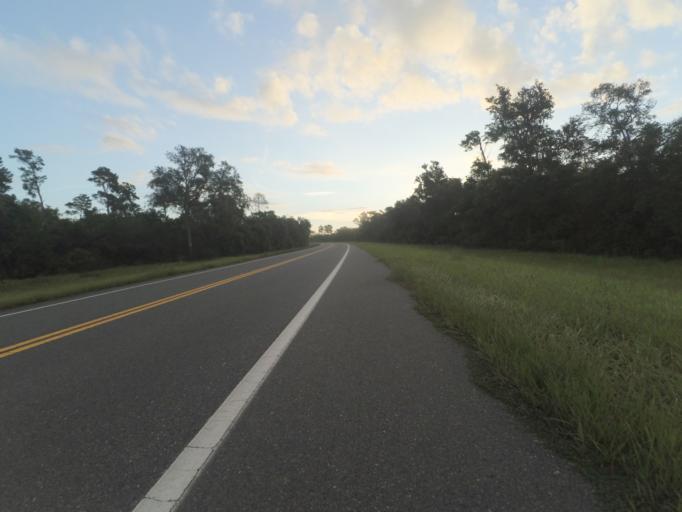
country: US
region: Florida
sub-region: Lake County
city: Astor
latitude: 29.2148
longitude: -81.6507
